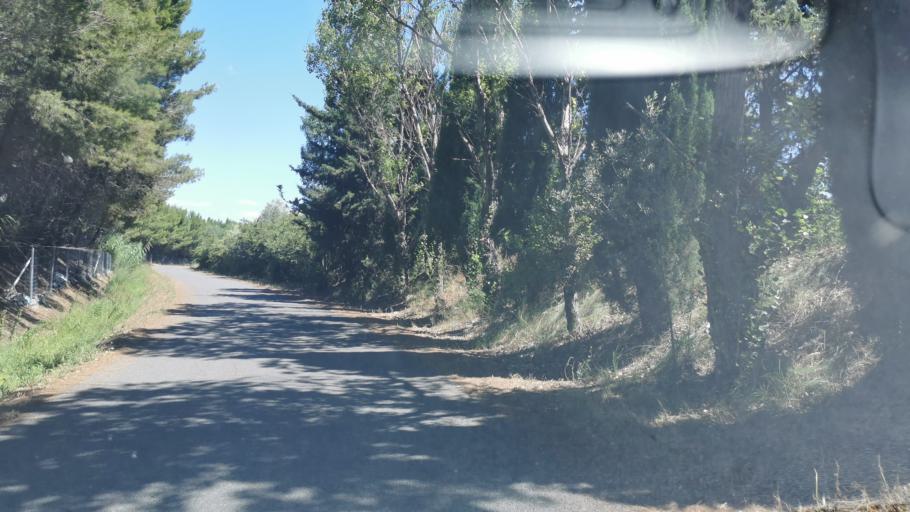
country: FR
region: Languedoc-Roussillon
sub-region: Departement de l'Aude
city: Narbonne
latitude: 43.1629
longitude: 2.9964
